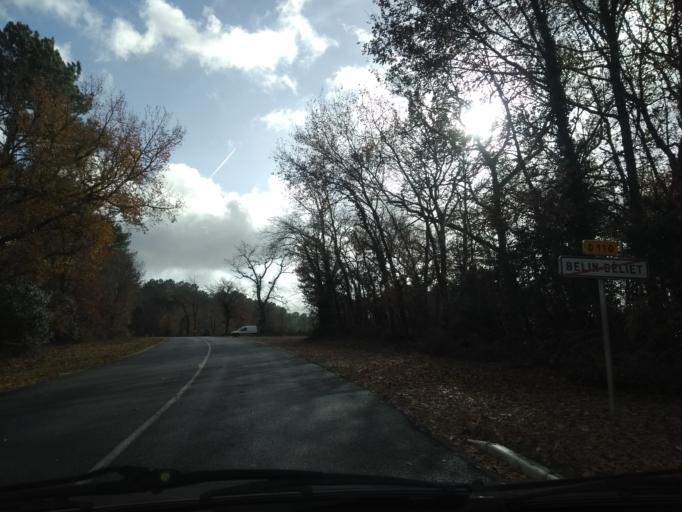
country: FR
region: Aquitaine
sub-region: Departement de la Gironde
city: Belin-Beliet
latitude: 44.4898
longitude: -0.7807
